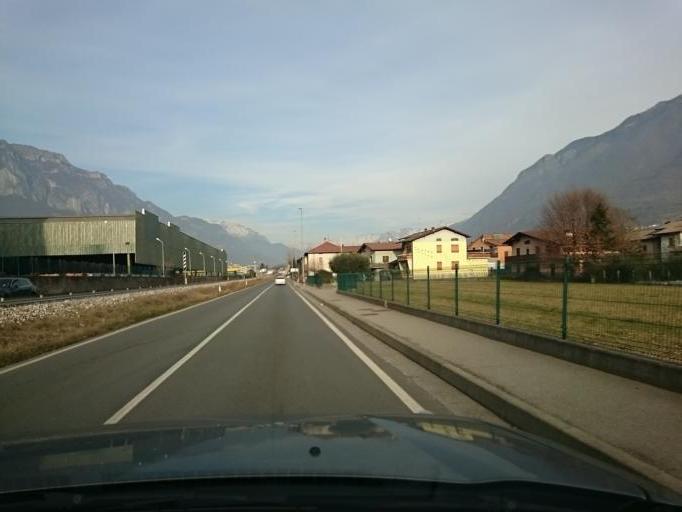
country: IT
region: Lombardy
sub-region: Provincia di Brescia
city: Gianico
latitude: 45.8645
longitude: 10.1653
